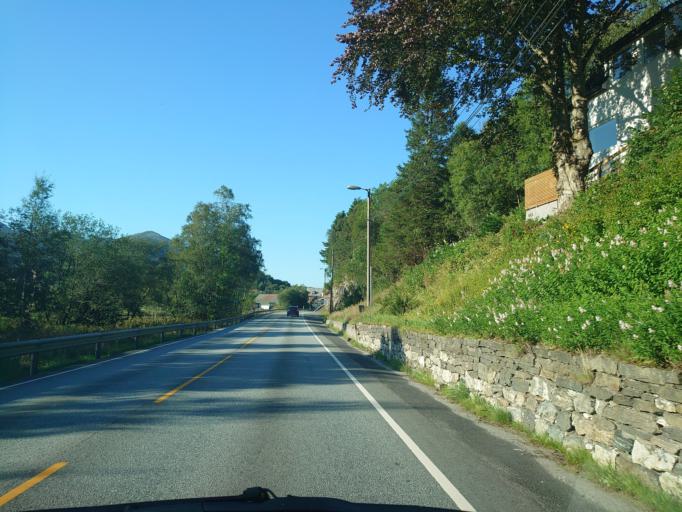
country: NO
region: Hordaland
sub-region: Bergen
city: Espeland
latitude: 60.3712
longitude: 5.4550
